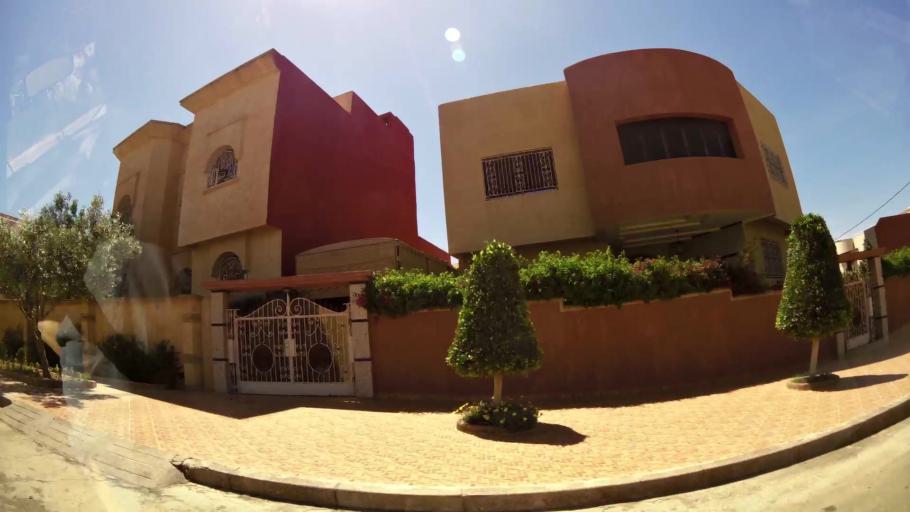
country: MA
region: Oriental
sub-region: Oujda-Angad
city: Oujda
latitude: 34.6528
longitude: -1.9156
